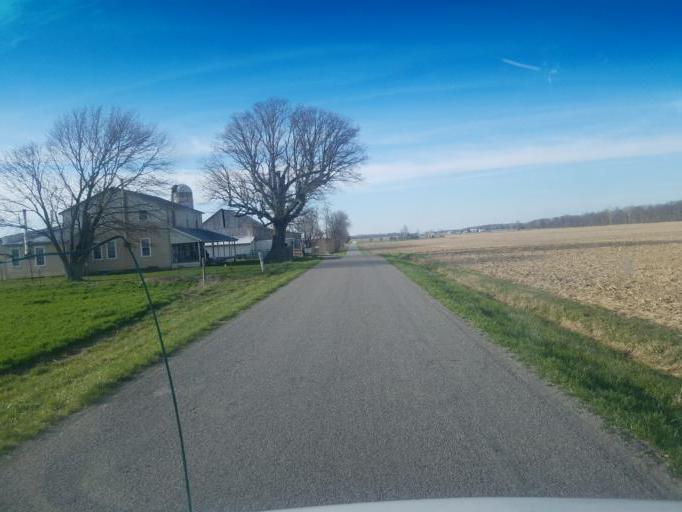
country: US
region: Ohio
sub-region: Logan County
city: De Graff
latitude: 40.3425
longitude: -83.9614
